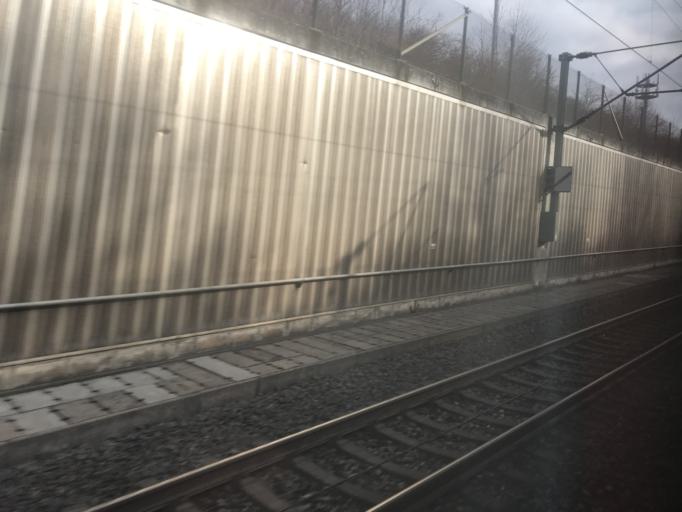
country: DE
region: Baden-Wuerttemberg
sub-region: Regierungsbezirk Stuttgart
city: Moglingen
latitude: 48.8719
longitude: 9.1327
